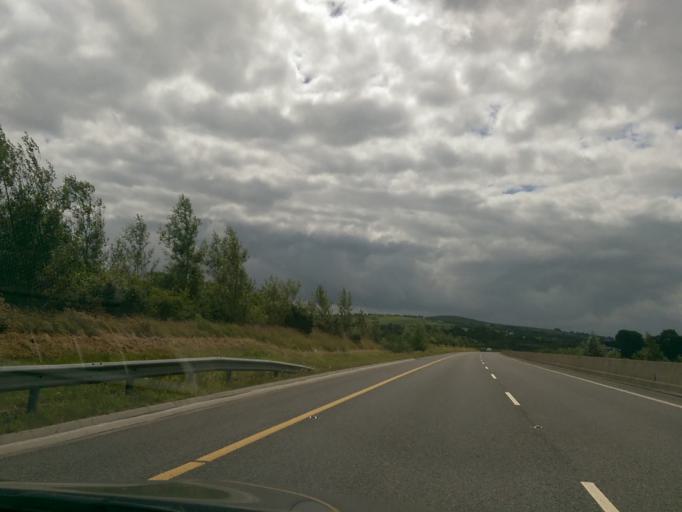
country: IE
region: Munster
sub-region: County Cork
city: Mitchelstown
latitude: 52.2625
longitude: -8.2489
